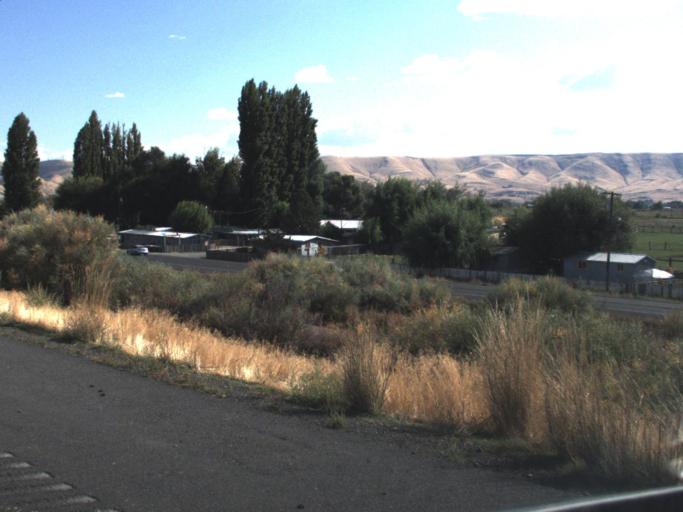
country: US
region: Washington
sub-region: Yakima County
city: Grandview
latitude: 46.2431
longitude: -119.8384
